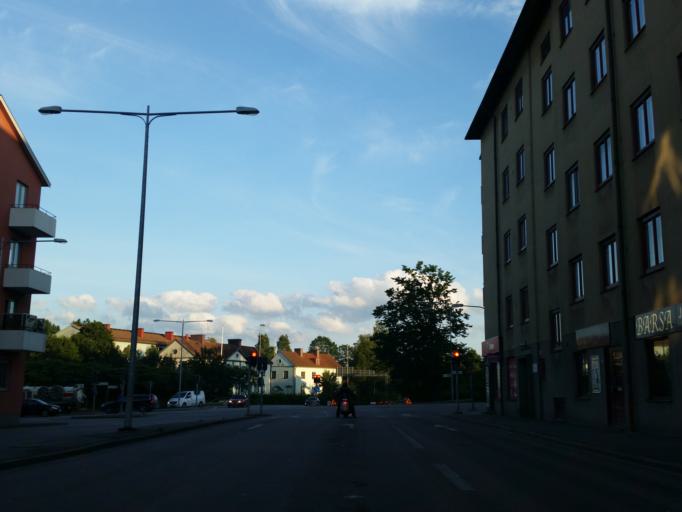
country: SE
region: Stockholm
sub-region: Sodertalje Kommun
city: Soedertaelje
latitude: 59.1982
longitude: 17.6197
